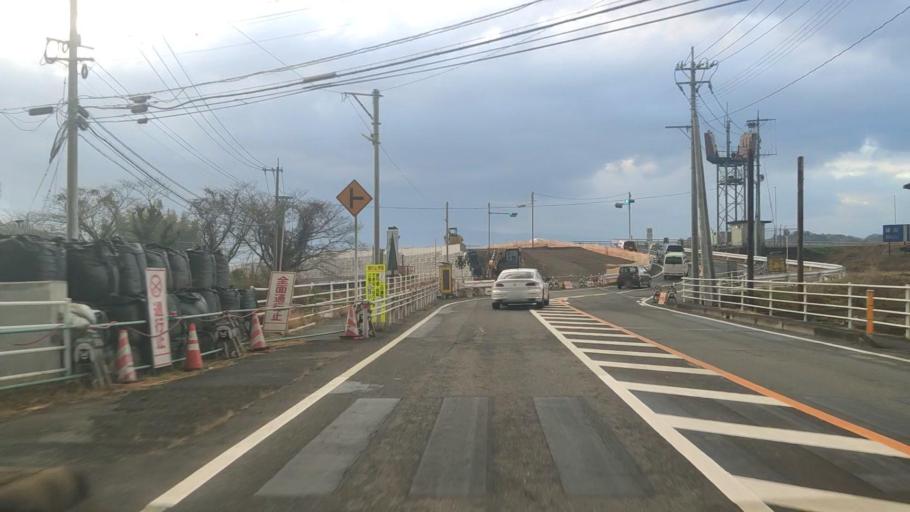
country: JP
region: Kumamoto
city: Uto
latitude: 32.7031
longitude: 130.7788
